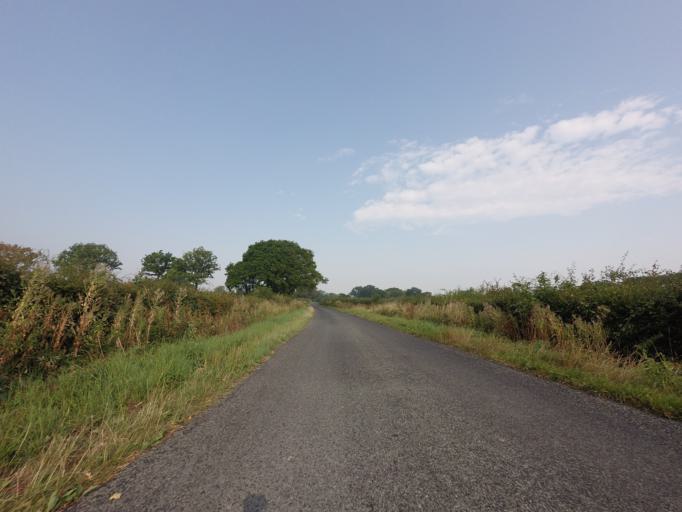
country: GB
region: England
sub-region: Kent
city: Headcorn
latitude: 51.1271
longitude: 0.6615
